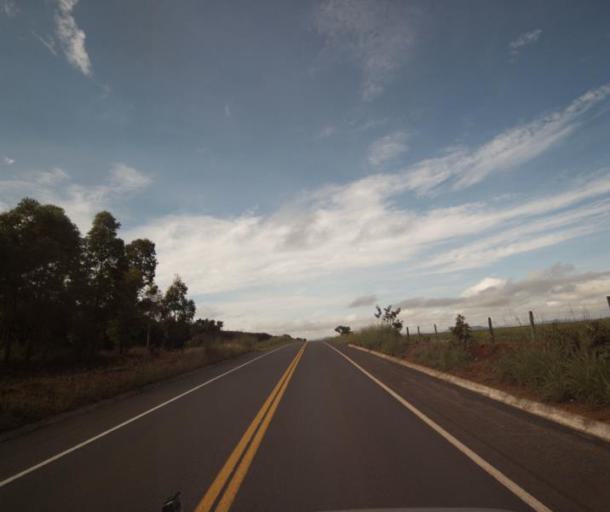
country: BR
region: Goias
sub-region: Padre Bernardo
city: Padre Bernardo
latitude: -15.3709
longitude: -48.6457
